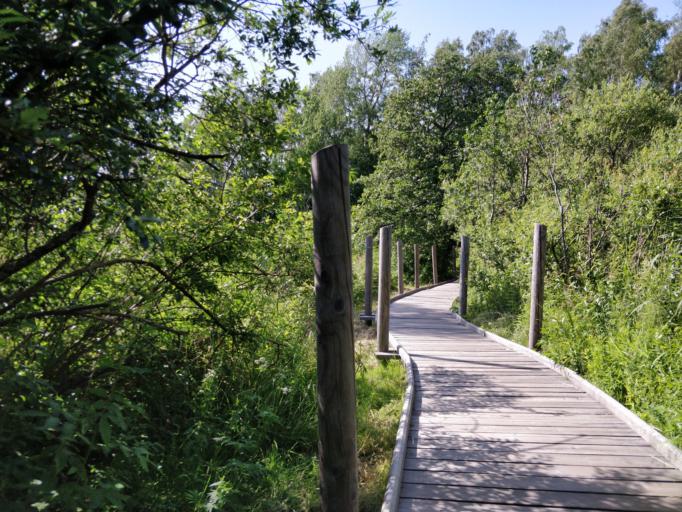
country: FI
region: Uusimaa
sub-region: Helsinki
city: Helsinki
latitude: 60.2122
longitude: 24.9892
